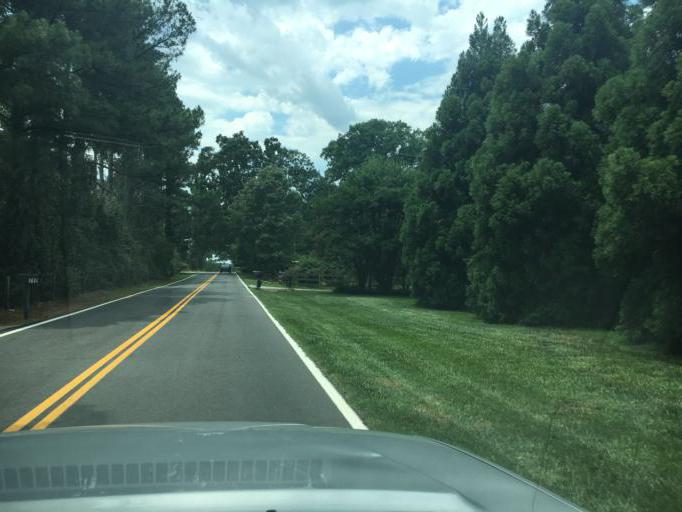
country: US
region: South Carolina
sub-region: Greenville County
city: Five Forks
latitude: 34.8703
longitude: -82.2097
